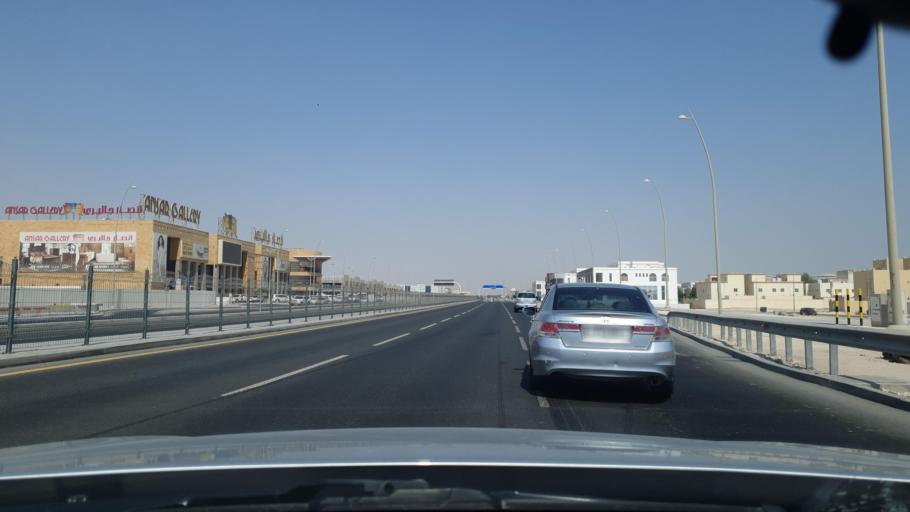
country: QA
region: Al Khawr
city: Al Khawr
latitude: 25.6643
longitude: 51.5010
